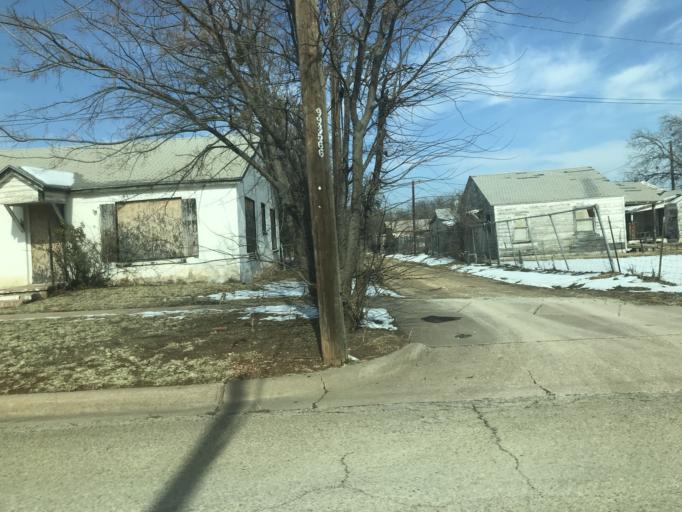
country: US
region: Texas
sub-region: Taylor County
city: Abilene
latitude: 32.4570
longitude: -99.7278
